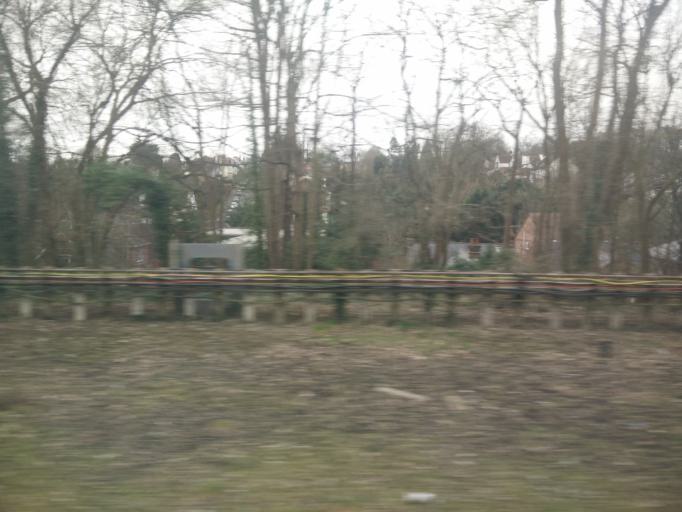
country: GB
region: England
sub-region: Hertfordshire
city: Chorleywood
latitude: 51.6548
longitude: -0.5194
